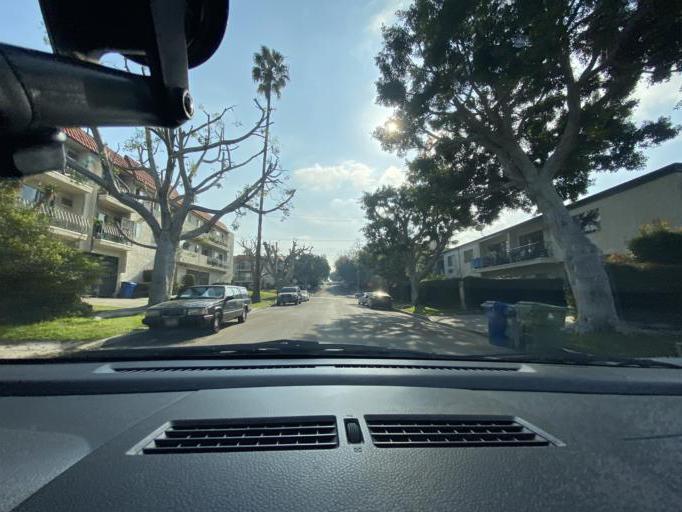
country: US
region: California
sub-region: Los Angeles County
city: Culver City
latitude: 34.0224
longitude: -118.4227
